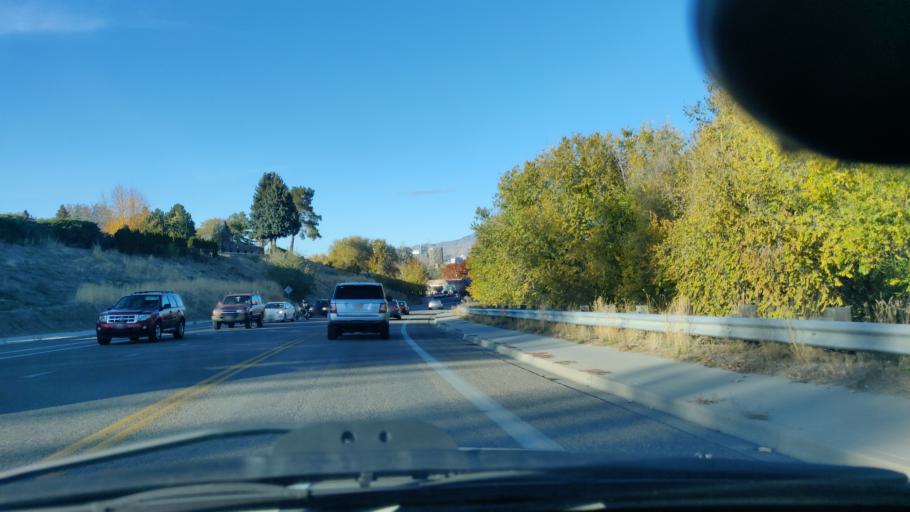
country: US
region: Idaho
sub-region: Ada County
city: Boise
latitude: 43.5954
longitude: -116.2061
